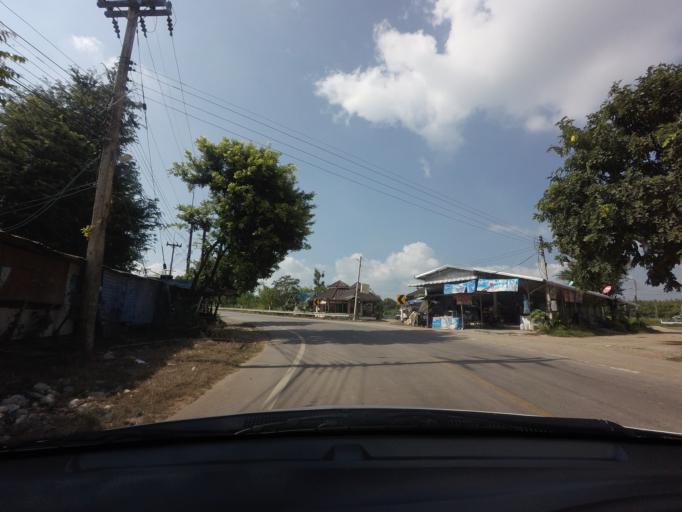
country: TH
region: Nakhon Ratchasima
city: Wang Nam Khiao
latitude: 14.4629
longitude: 101.6563
